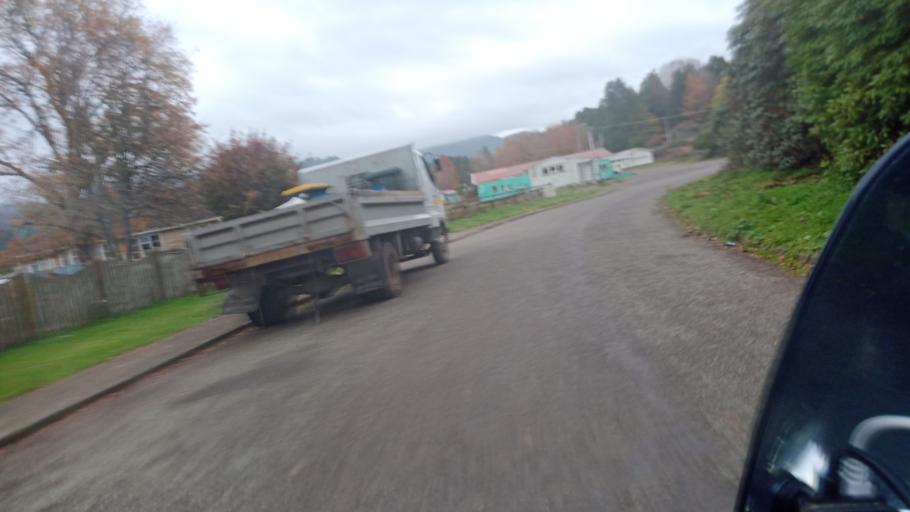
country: NZ
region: Bay of Plenty
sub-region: Whakatane District
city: Murupara
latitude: -38.6406
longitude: 176.7308
